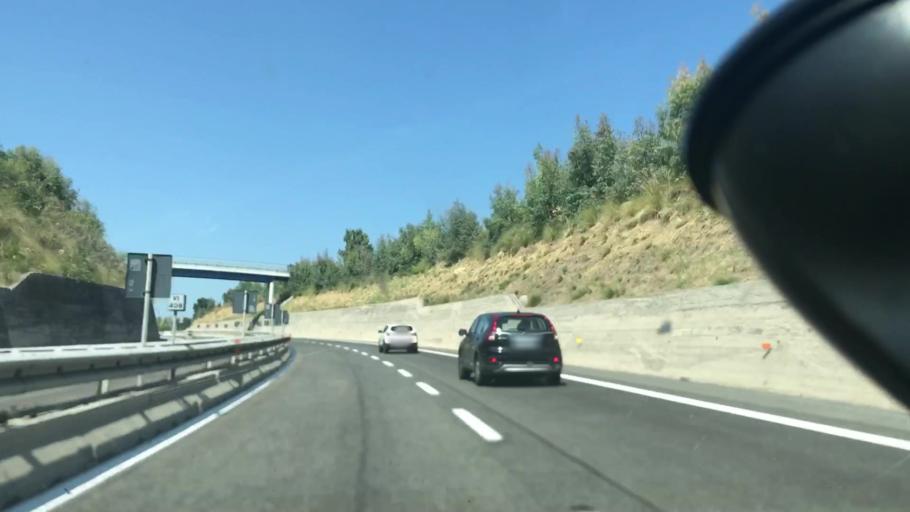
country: IT
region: Abruzzo
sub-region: Provincia di Chieti
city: San Vito Chietino
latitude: 42.2979
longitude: 14.4317
